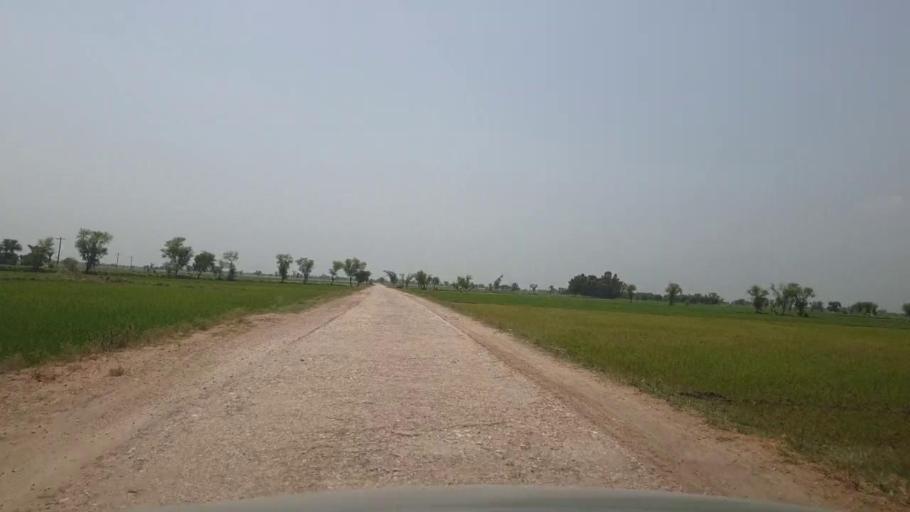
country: PK
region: Sindh
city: Garhi Yasin
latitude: 27.9229
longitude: 68.4040
